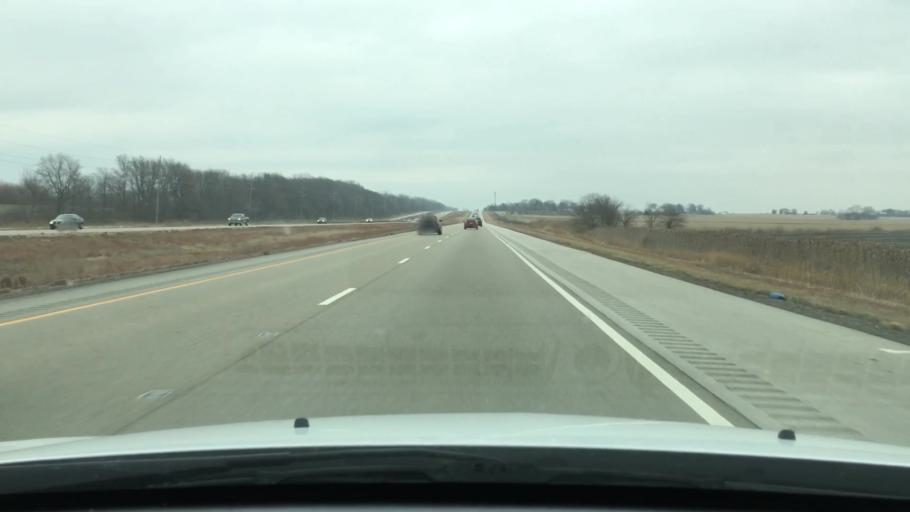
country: US
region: Illinois
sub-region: Logan County
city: Atlanta
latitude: 40.2292
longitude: -89.2671
